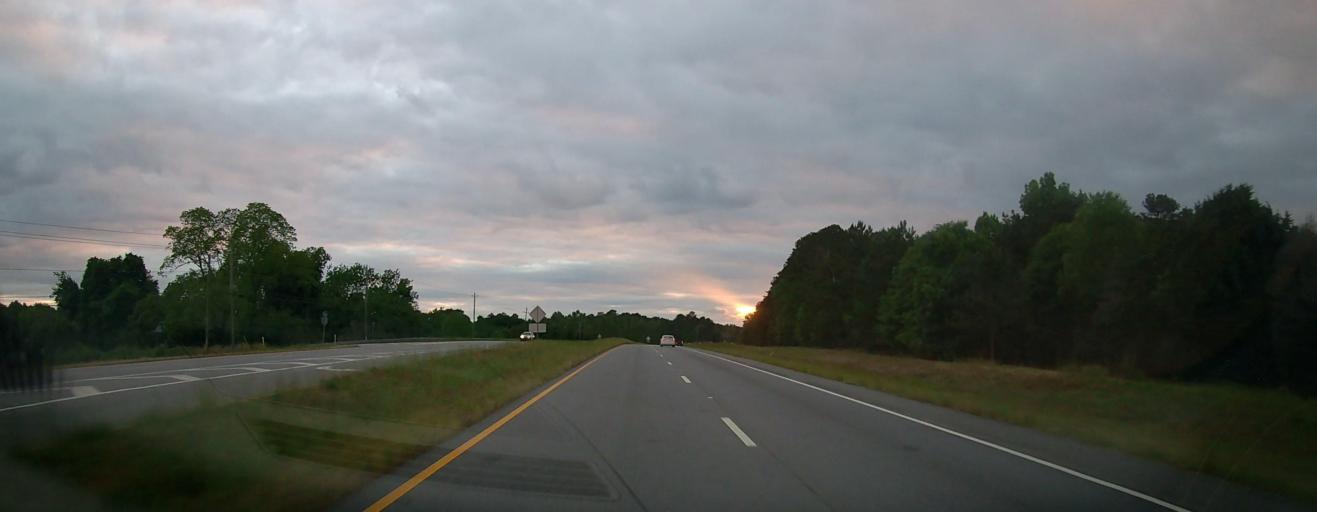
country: US
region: Georgia
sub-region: Clarke County
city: Country Club Estates
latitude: 34.0094
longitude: -83.4716
